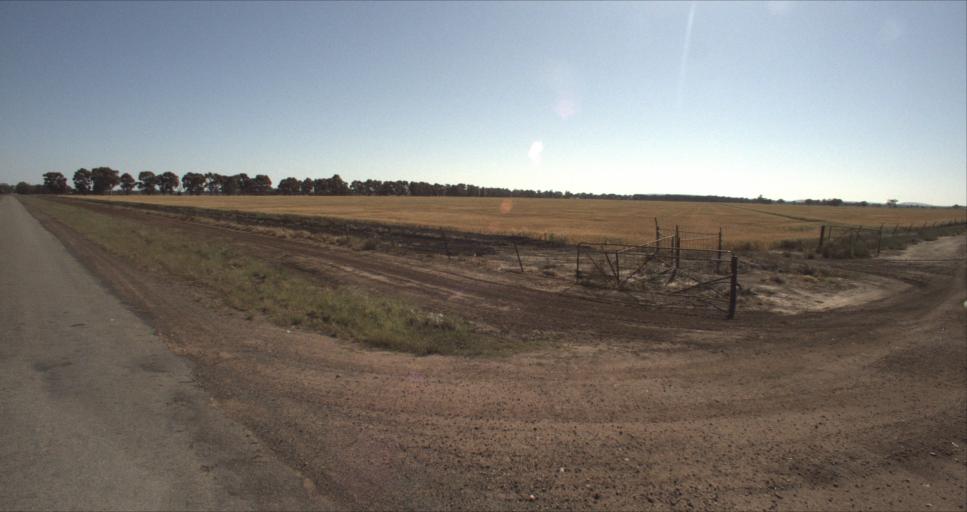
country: AU
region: New South Wales
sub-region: Leeton
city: Leeton
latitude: -34.5541
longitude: 146.3140
